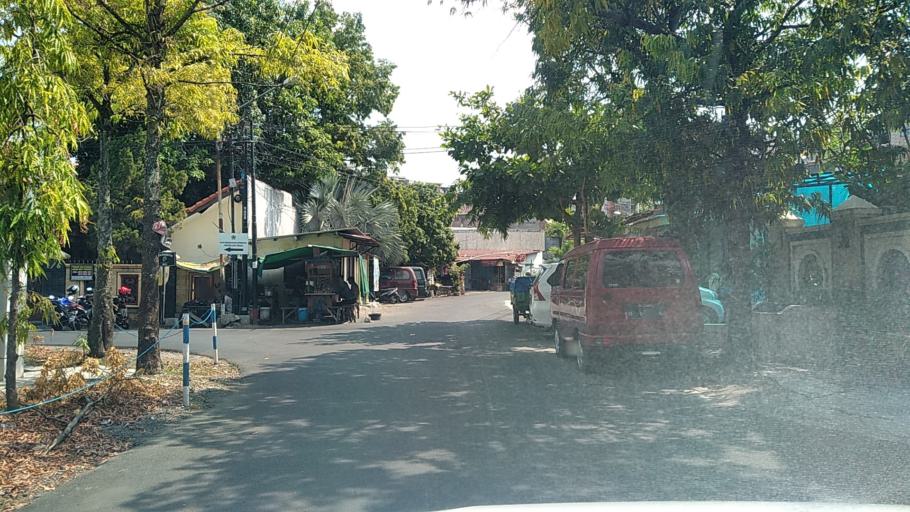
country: ID
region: Central Java
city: Semarang
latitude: -6.9943
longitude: 110.4169
